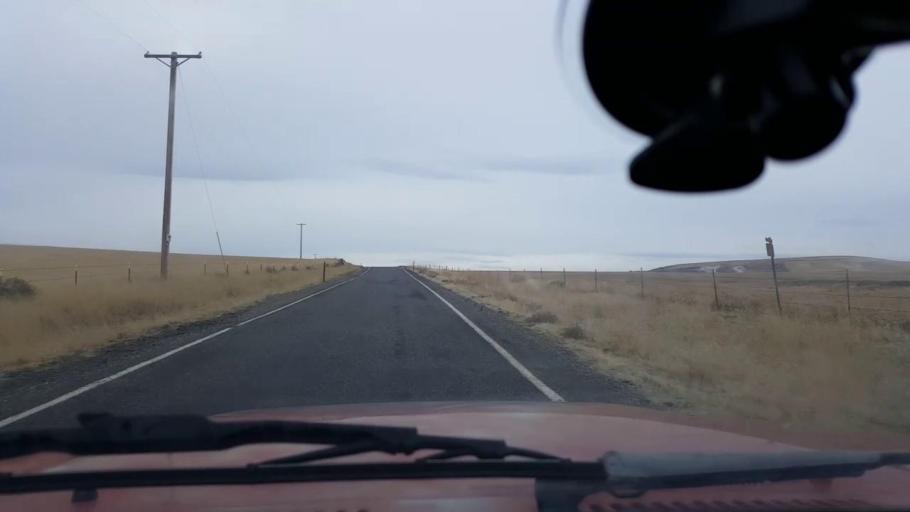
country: US
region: Washington
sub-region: Asotin County
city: Clarkston Heights-Vineland
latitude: 46.3301
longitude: -117.3208
